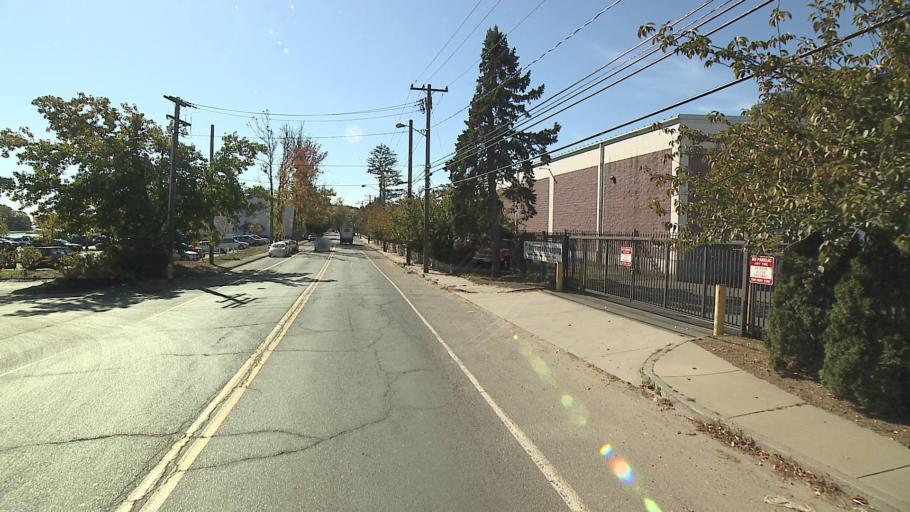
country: US
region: Connecticut
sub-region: Fairfield County
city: East Norwalk
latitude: 41.0825
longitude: -73.4224
